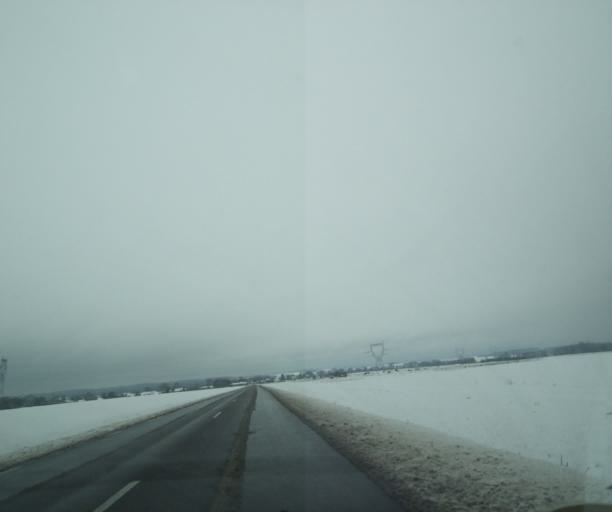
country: FR
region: Champagne-Ardenne
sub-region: Departement de la Haute-Marne
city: Montier-en-Der
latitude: 48.4990
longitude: 4.7853
